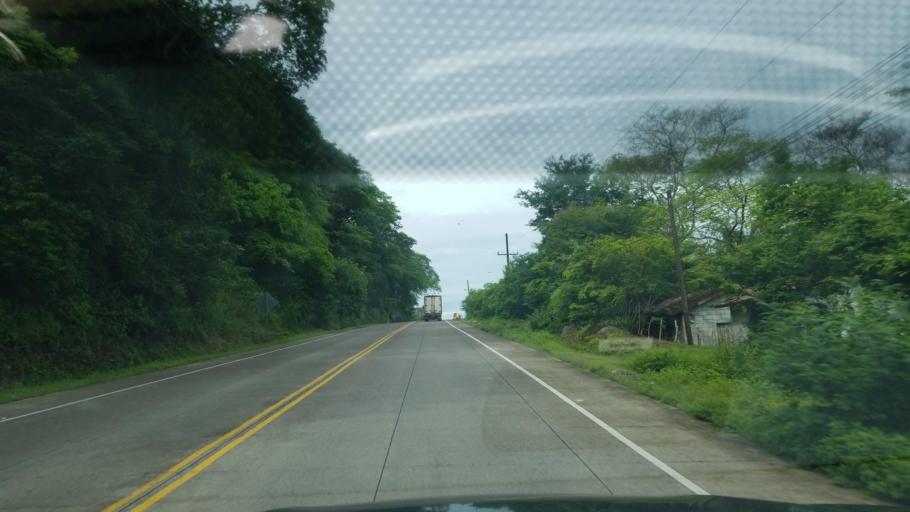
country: HN
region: Choluteca
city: Pespire
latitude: 13.6325
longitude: -87.3691
